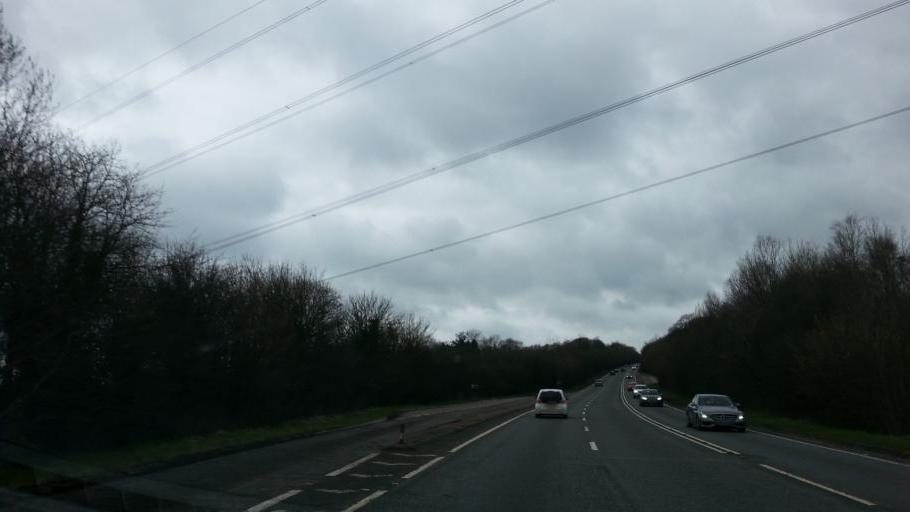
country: GB
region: England
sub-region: Devon
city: South Molton
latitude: 51.0166
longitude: -3.7909
